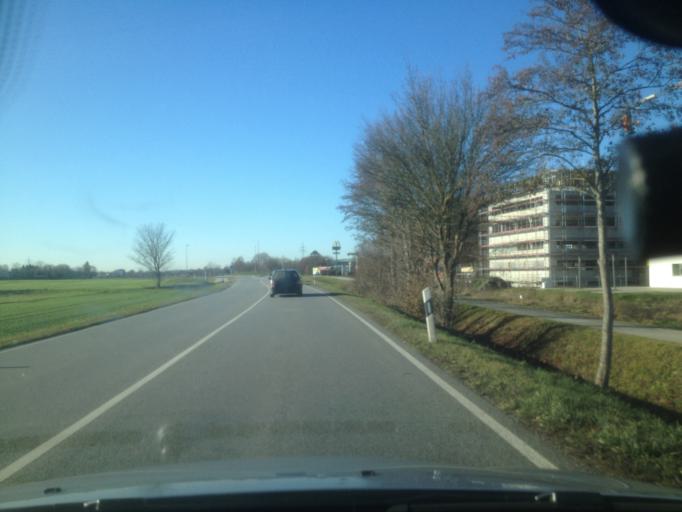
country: DE
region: Bavaria
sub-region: Lower Bavaria
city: Tiefenbach
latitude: 48.5389
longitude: 12.0993
